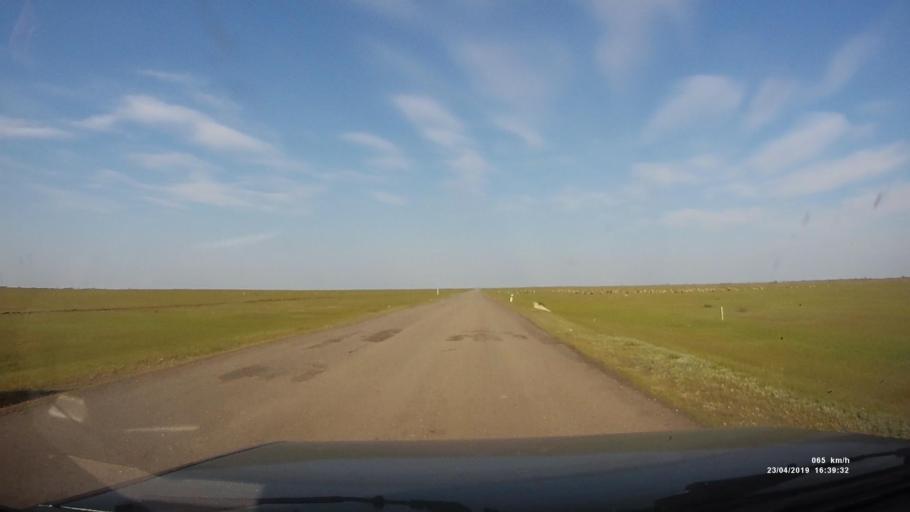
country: RU
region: Kalmykiya
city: Priyutnoye
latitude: 46.3398
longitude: 43.1669
